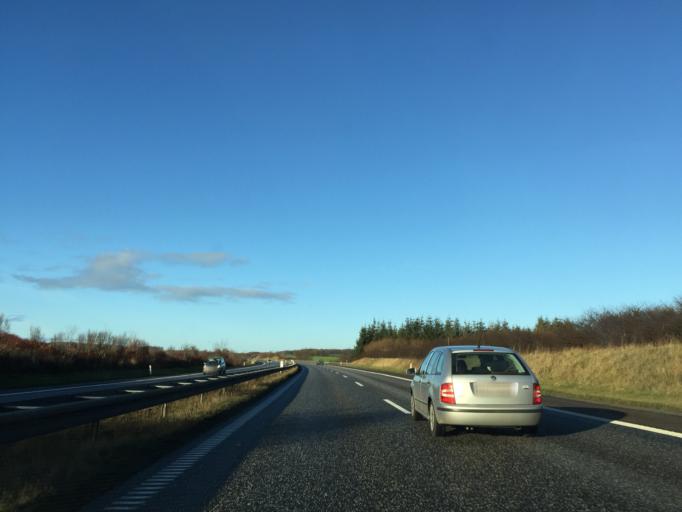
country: DK
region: South Denmark
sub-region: Fredericia Kommune
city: Taulov
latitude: 55.5857
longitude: 9.6087
